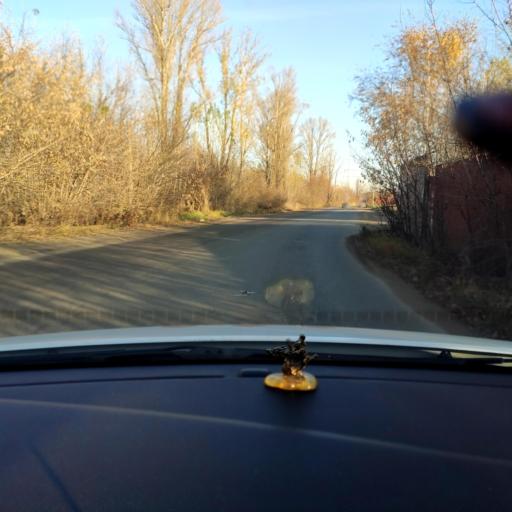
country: RU
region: Tatarstan
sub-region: Gorod Kazan'
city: Kazan
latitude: 55.7757
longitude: 49.0959
